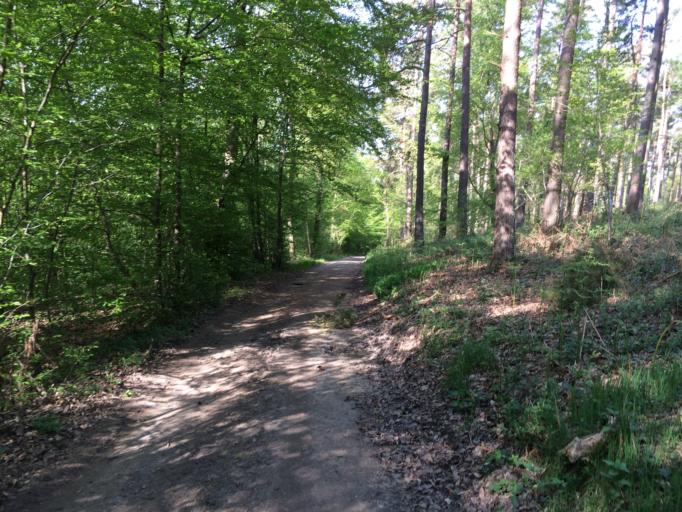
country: BE
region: Wallonia
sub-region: Province de Namur
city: Assesse
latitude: 50.3361
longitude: 4.9552
